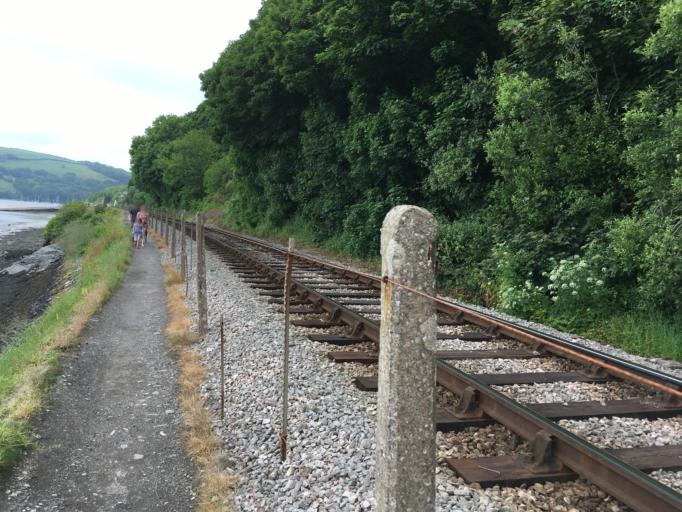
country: GB
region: England
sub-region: Devon
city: Dartmouth
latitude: 50.3573
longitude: -3.5707
